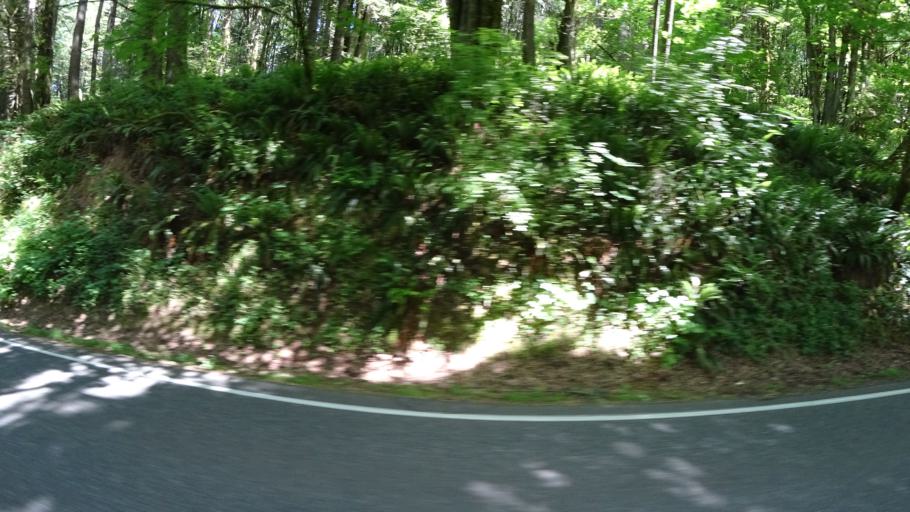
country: US
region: Oregon
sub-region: Washington County
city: Oak Hills
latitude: 45.5858
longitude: -122.7984
